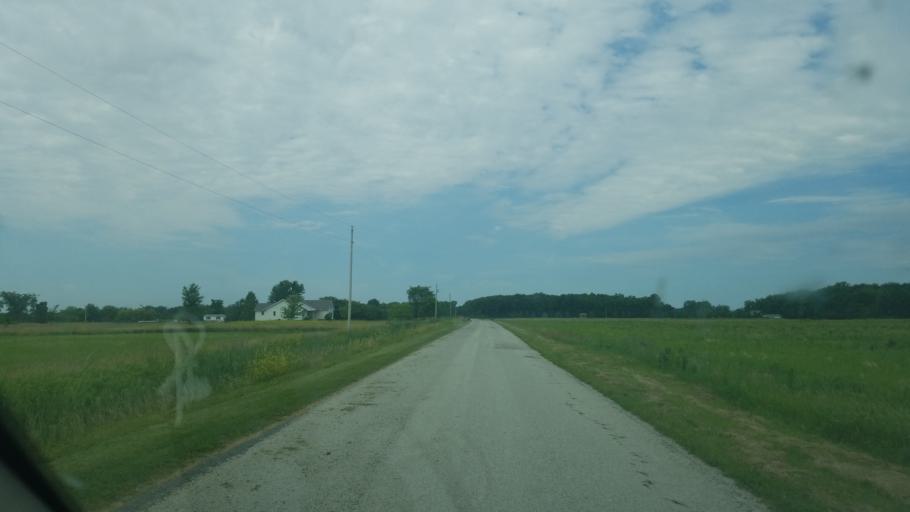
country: US
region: Ohio
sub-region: Wood County
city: North Baltimore
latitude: 41.2329
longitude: -83.6089
